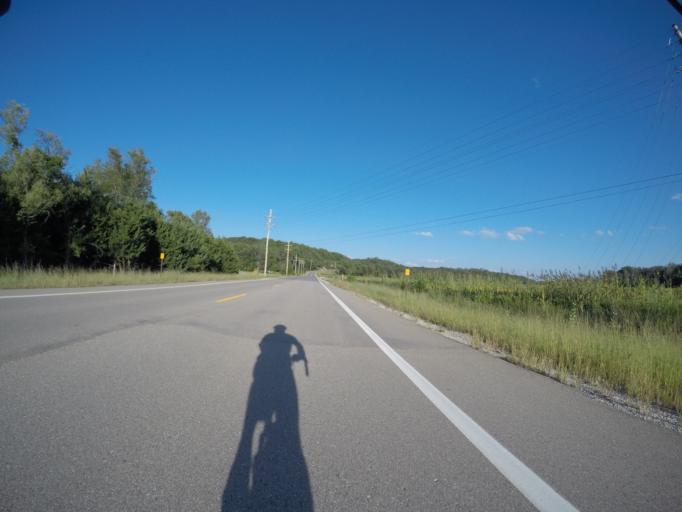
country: US
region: Kansas
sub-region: Riley County
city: Manhattan
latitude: 39.1577
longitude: -96.6246
